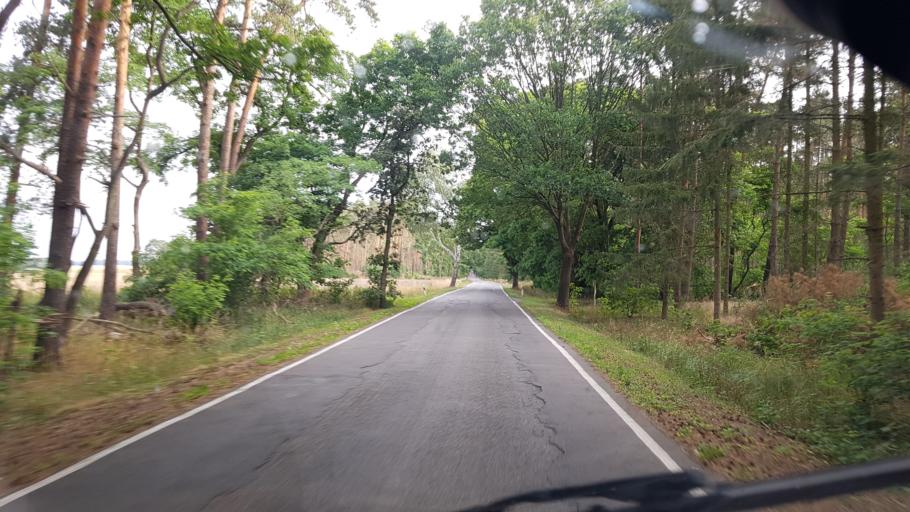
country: DE
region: Brandenburg
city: Dahme
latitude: 51.9330
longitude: 13.3969
